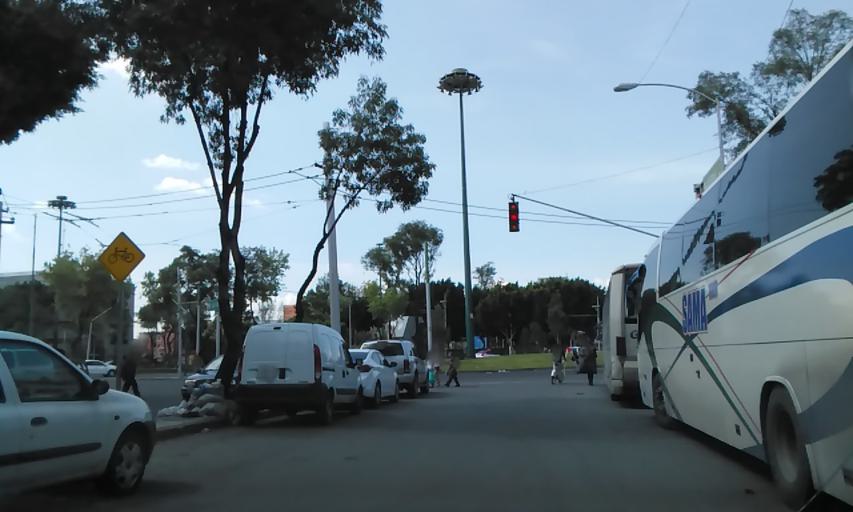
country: MX
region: Mexico City
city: Cuauhtemoc
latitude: 19.4395
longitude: -99.1434
